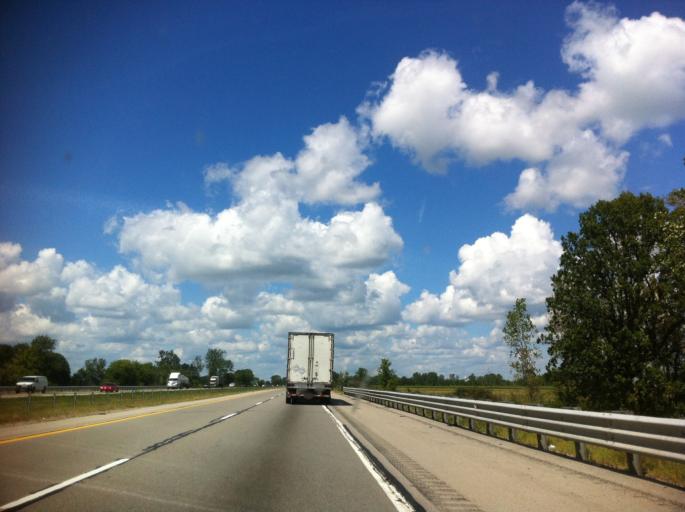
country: US
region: Michigan
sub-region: Monroe County
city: Dundee
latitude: 41.9855
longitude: -83.6783
